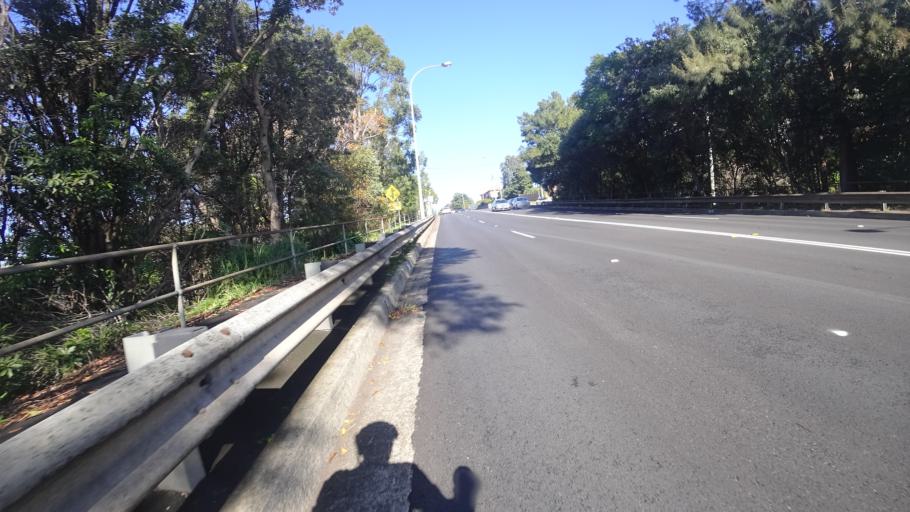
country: AU
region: New South Wales
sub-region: North Sydney
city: St Leonards
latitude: -33.8159
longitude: 151.2058
